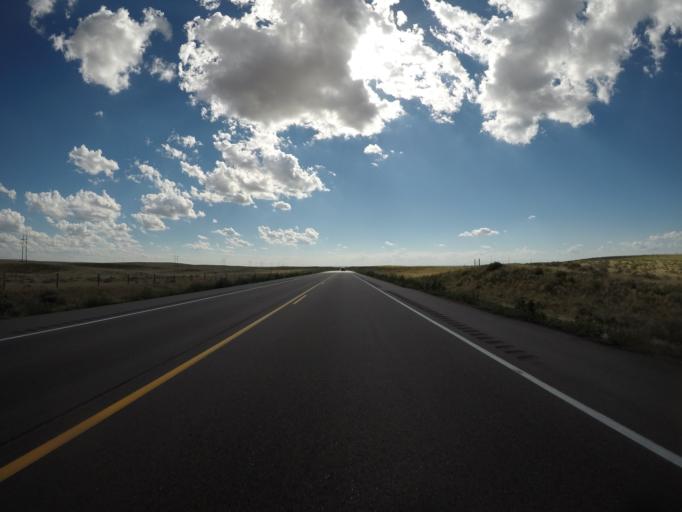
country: US
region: Colorado
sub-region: Logan County
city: Sterling
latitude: 40.6324
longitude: -103.1239
